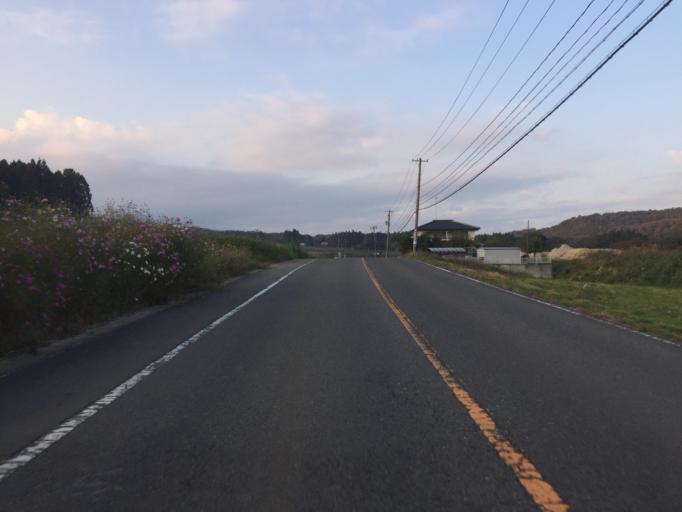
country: JP
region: Fukushima
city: Motomiya
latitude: 37.5631
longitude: 140.3514
